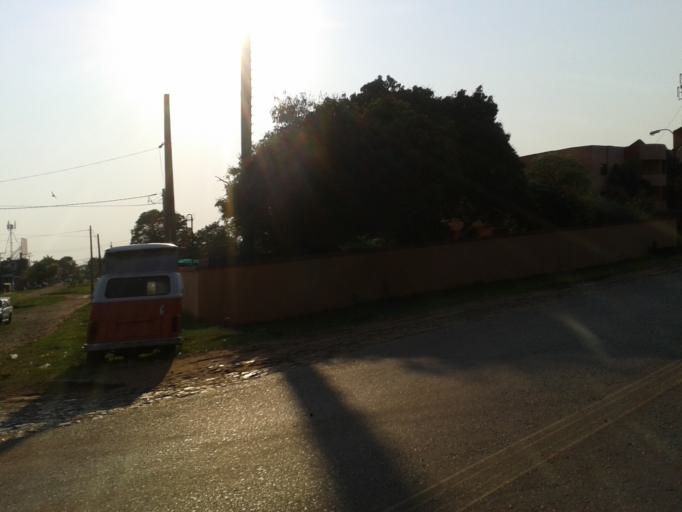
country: PY
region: Guaira
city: Villarrica
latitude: -25.7667
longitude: -56.4401
